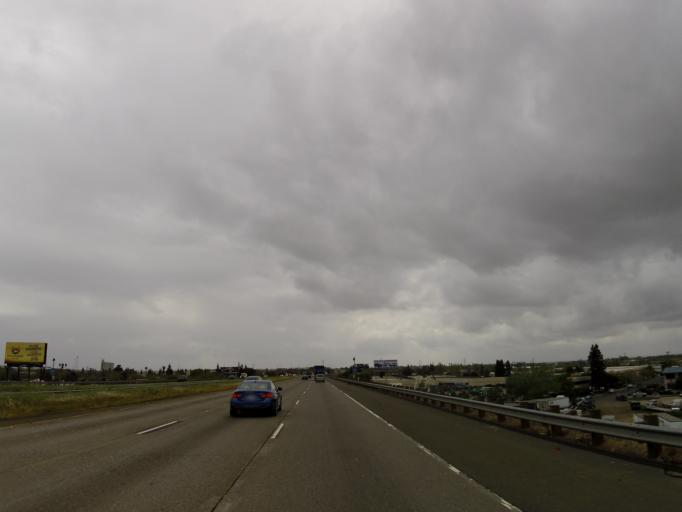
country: US
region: California
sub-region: Yolo County
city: West Sacramento
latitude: 38.5836
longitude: -121.5581
